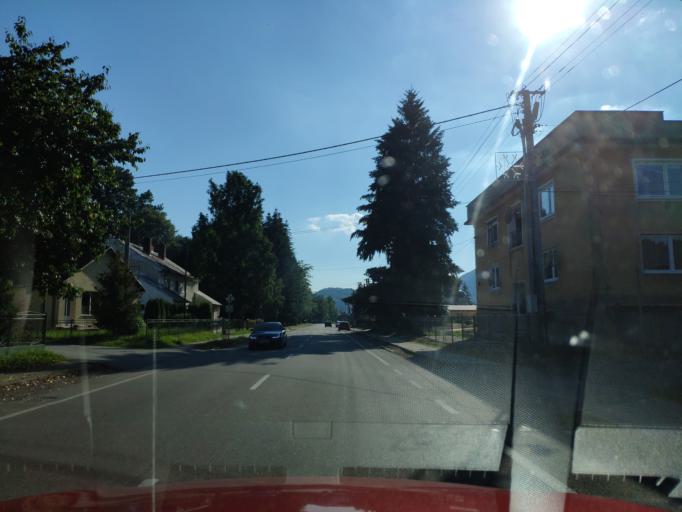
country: SK
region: Presovsky
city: Snina
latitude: 49.0021
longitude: 22.2305
